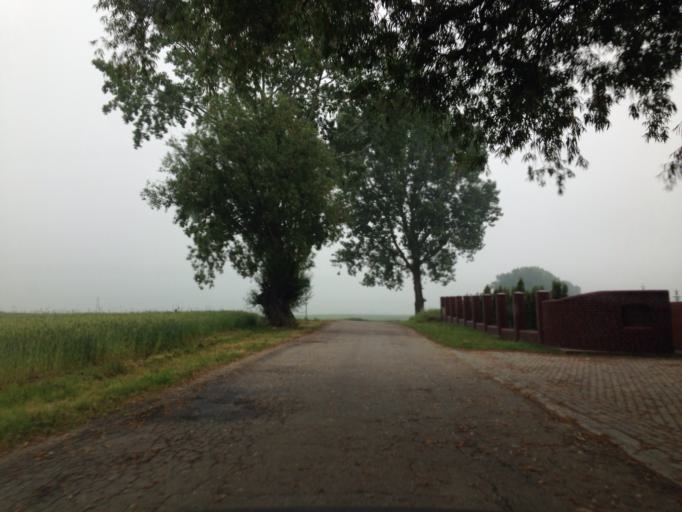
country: PL
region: Kujawsko-Pomorskie
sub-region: Powiat brodnicki
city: Jablonowo Pomorskie
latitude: 53.3950
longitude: 19.2302
